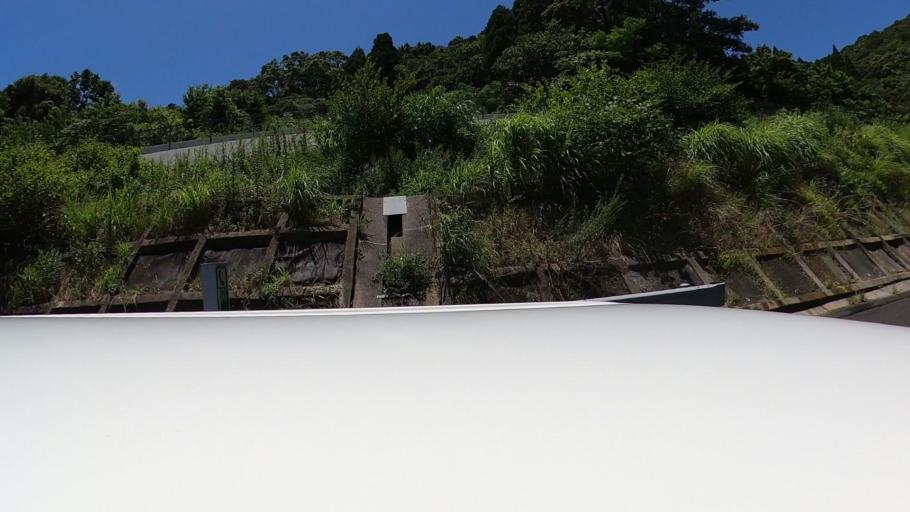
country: JP
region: Miyazaki
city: Nobeoka
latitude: 32.4063
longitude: 131.6131
